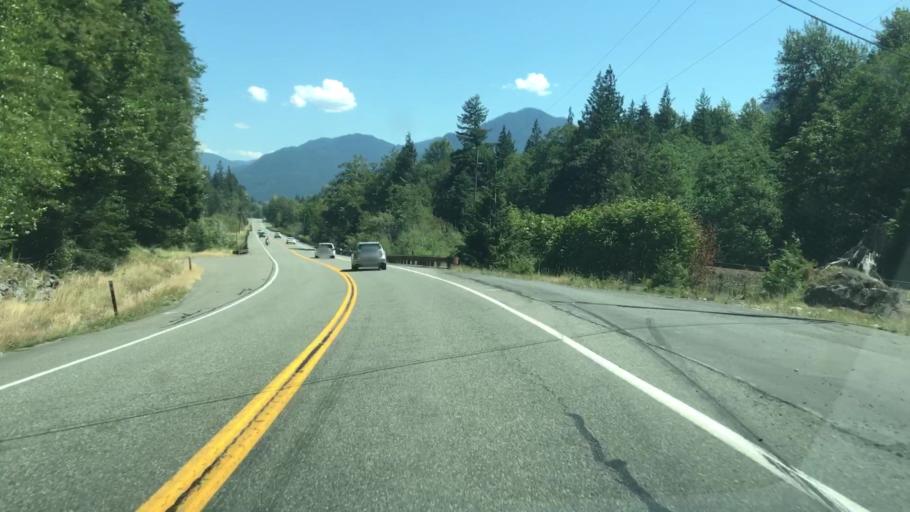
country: US
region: Washington
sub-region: Snohomish County
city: Gold Bar
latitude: 47.7414
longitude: -121.4384
